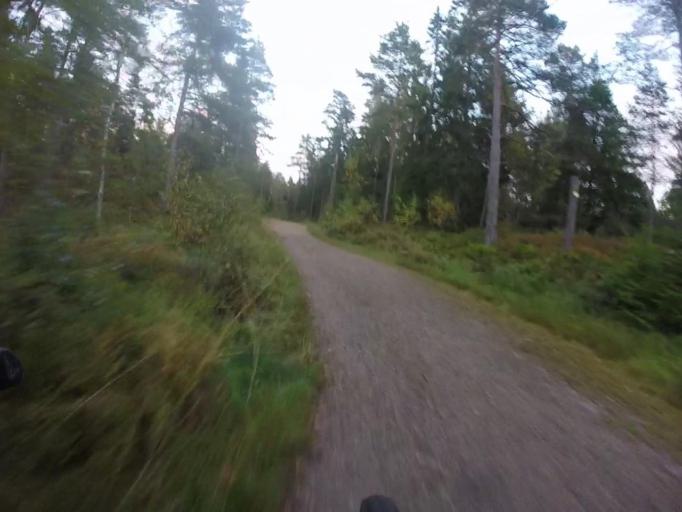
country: SE
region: Vaestra Goetaland
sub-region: Trollhattan
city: Trollhattan
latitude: 58.2949
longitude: 12.2567
